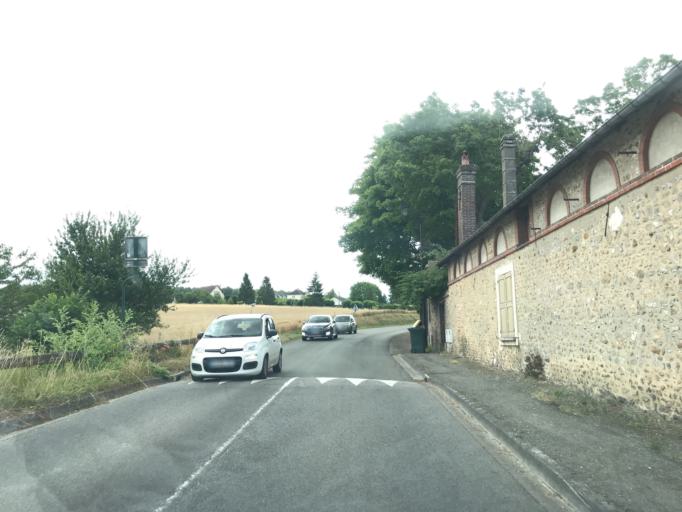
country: FR
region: Haute-Normandie
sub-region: Departement de l'Eure
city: Houlbec-Cocherel
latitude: 49.0732
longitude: 1.3095
